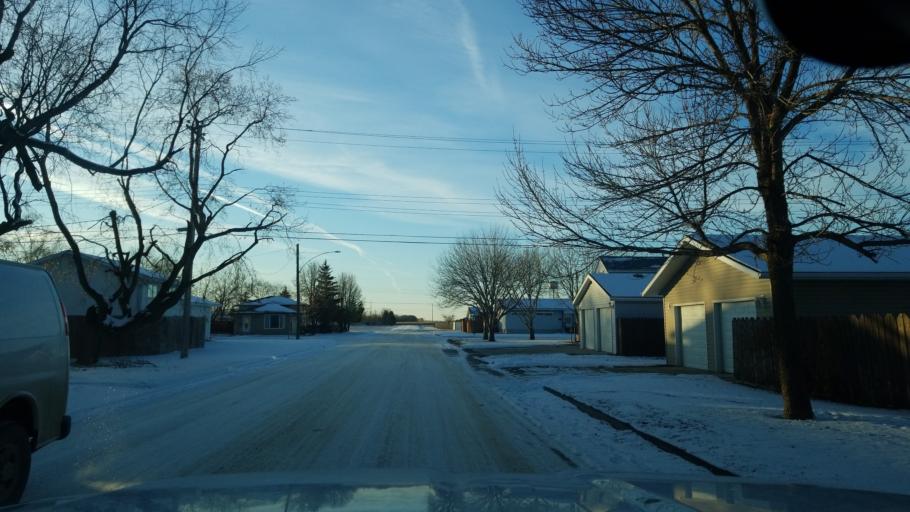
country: CA
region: Manitoba
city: Portage la Prairie
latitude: 49.9797
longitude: -98.3022
